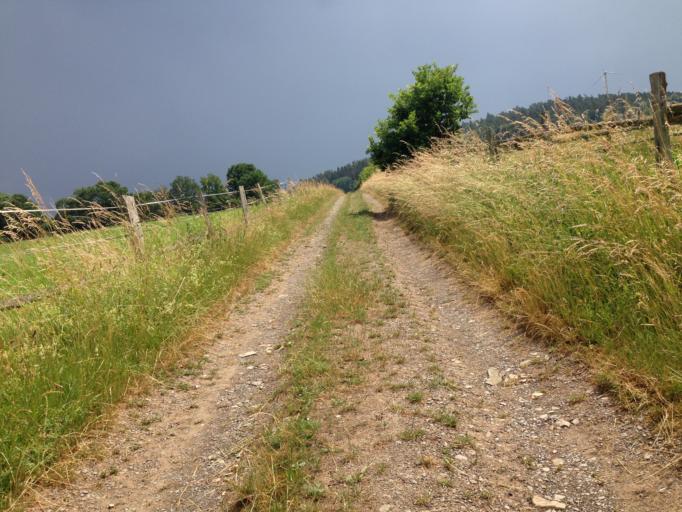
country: DE
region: Hesse
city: Wetter
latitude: 50.8612
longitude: 8.7386
